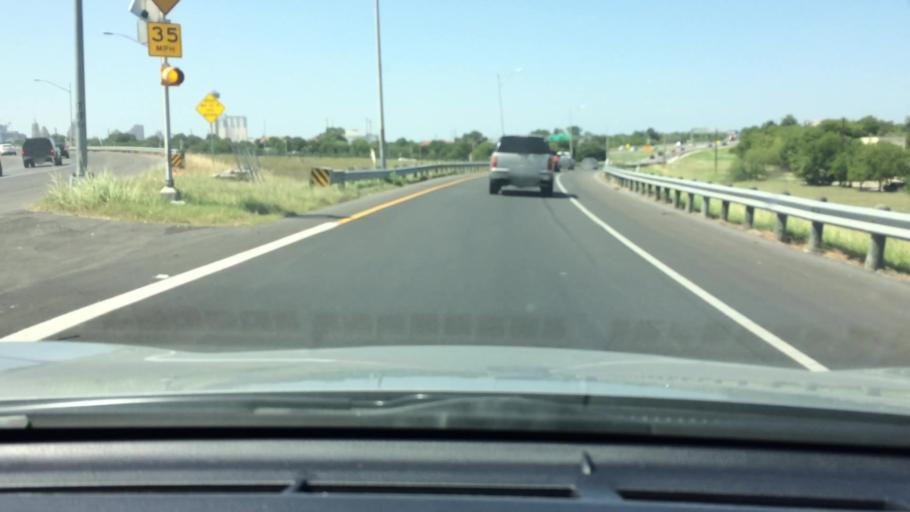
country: US
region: Texas
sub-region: Bexar County
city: San Antonio
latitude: 29.3933
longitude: -98.4767
